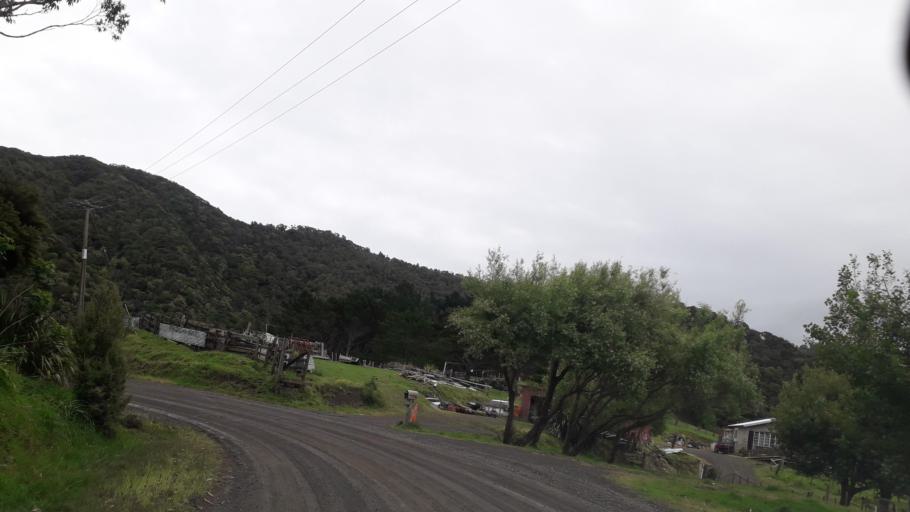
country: NZ
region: Northland
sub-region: Far North District
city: Ahipara
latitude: -35.4369
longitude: 173.3073
